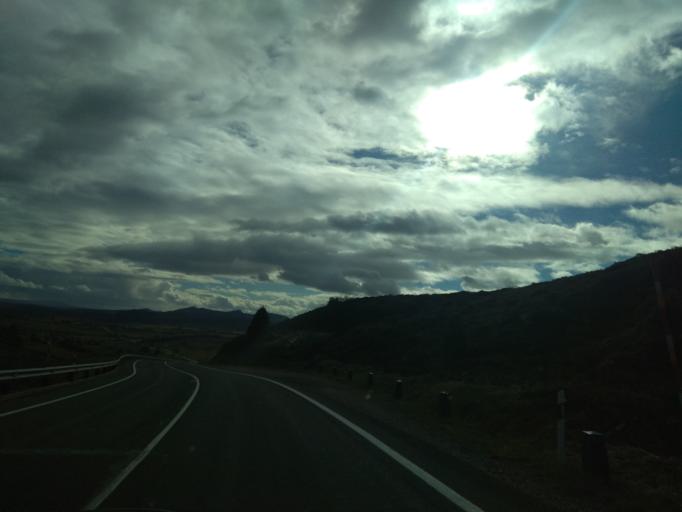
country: ES
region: Castille and Leon
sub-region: Provincia de Burgos
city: Arija
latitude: 43.0351
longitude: -3.8671
